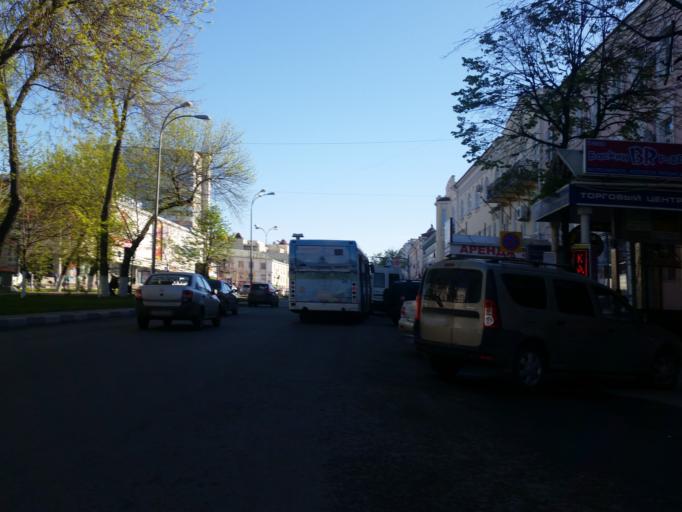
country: RU
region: Ulyanovsk
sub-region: Ulyanovskiy Rayon
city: Ulyanovsk
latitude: 54.3168
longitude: 48.3963
